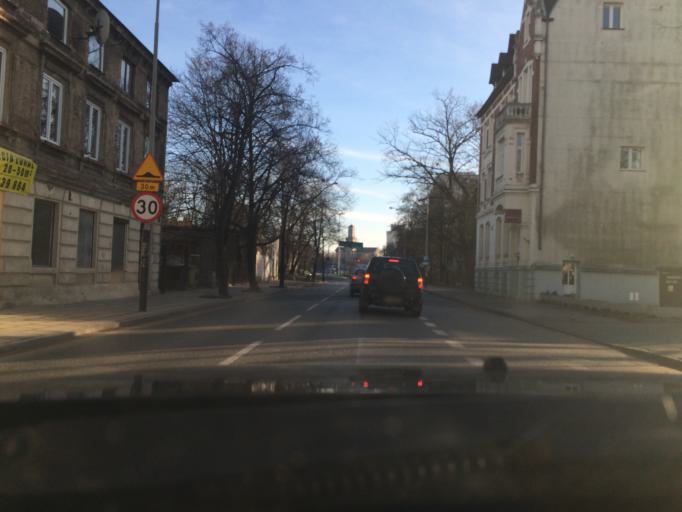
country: PL
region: Lodz Voivodeship
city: Lodz
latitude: 51.7623
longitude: 19.4405
